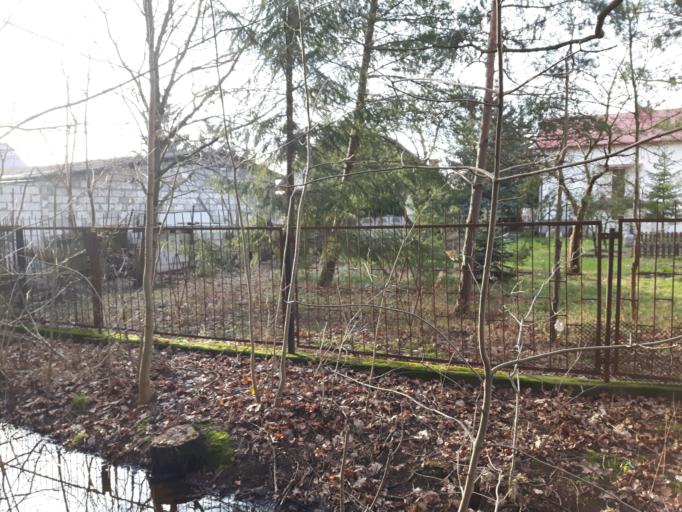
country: PL
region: Masovian Voivodeship
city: Zielonka
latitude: 52.2873
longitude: 21.1386
